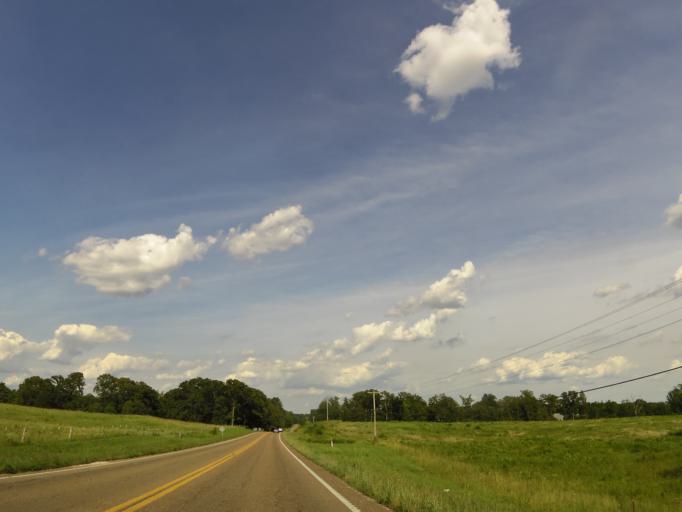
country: US
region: Tennessee
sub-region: Carroll County
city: Huntingdon
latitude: 36.0309
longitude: -88.3511
